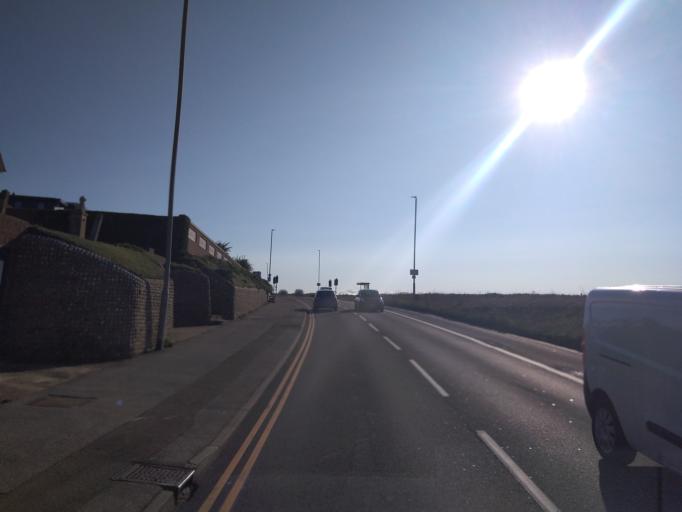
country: GB
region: England
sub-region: Brighton and Hove
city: Rottingdean
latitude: 50.8024
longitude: -0.0538
